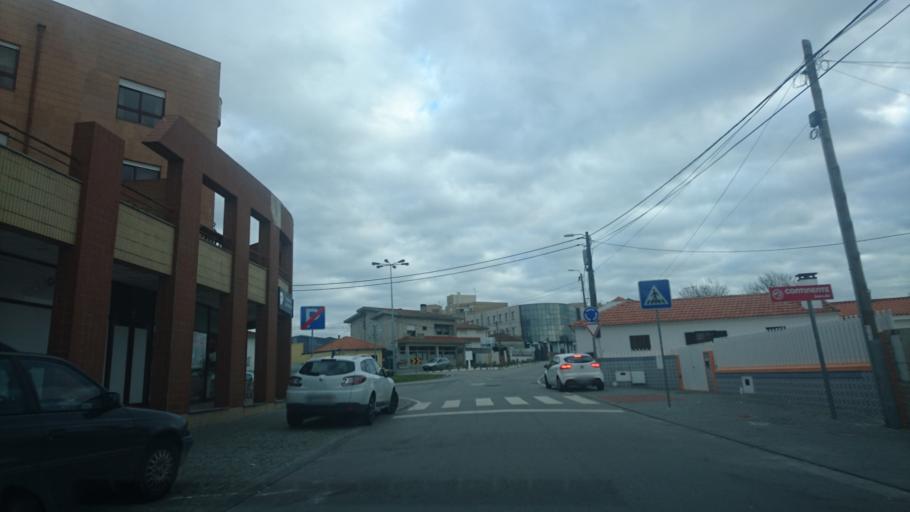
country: PT
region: Aveiro
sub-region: Santa Maria da Feira
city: Pacos de Brandao
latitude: 40.9744
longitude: -8.5798
